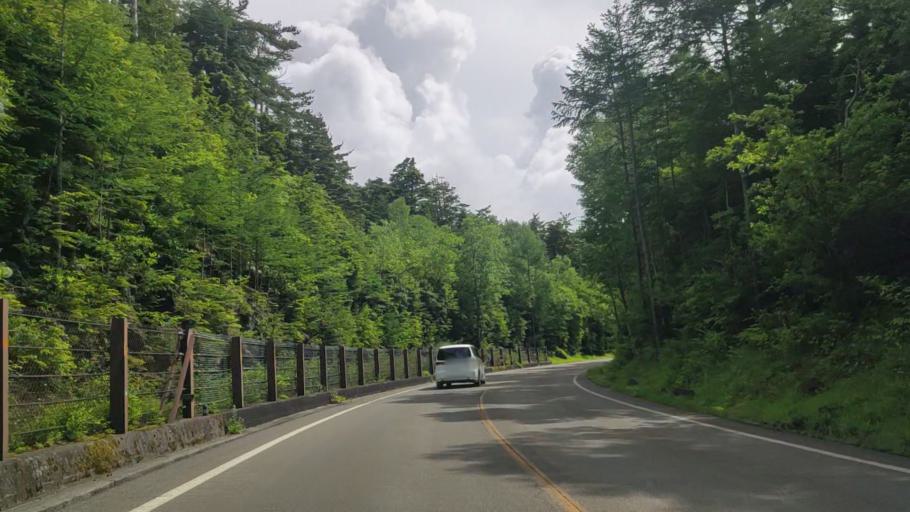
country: JP
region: Yamanashi
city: Fujikawaguchiko
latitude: 35.4106
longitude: 138.6998
